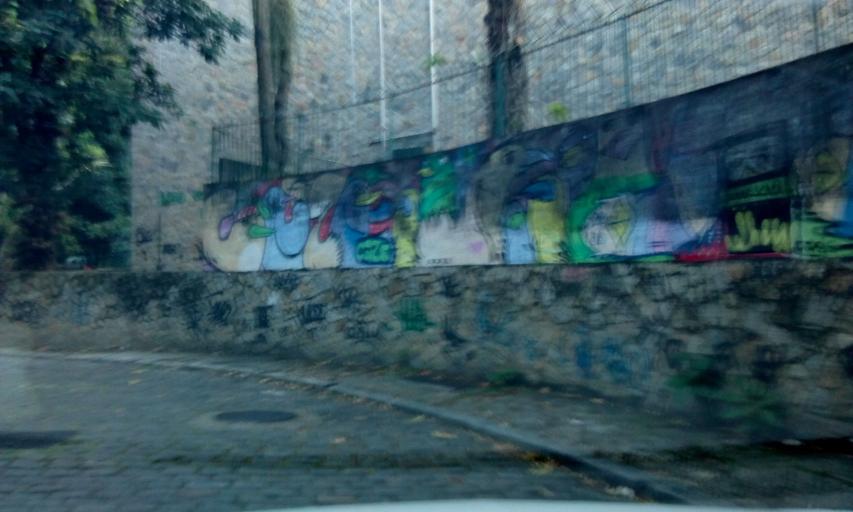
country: BR
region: Rio de Janeiro
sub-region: Rio De Janeiro
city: Rio de Janeiro
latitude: -22.9659
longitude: -43.2013
